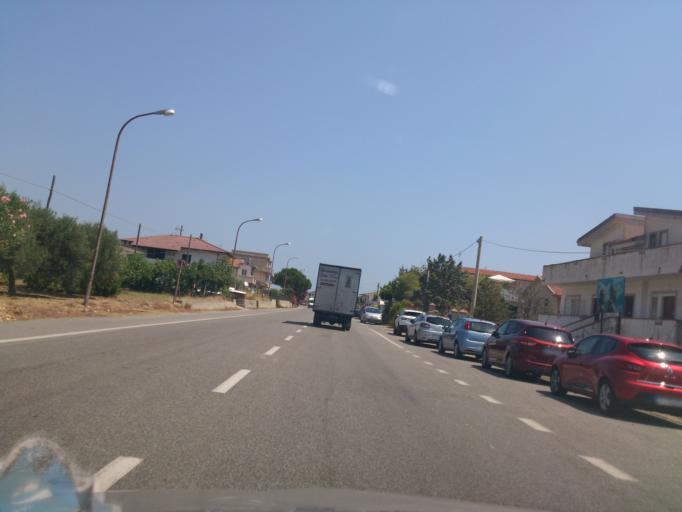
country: IT
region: Calabria
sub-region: Provincia di Reggio Calabria
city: Riace Marina
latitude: 38.3990
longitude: 16.5405
